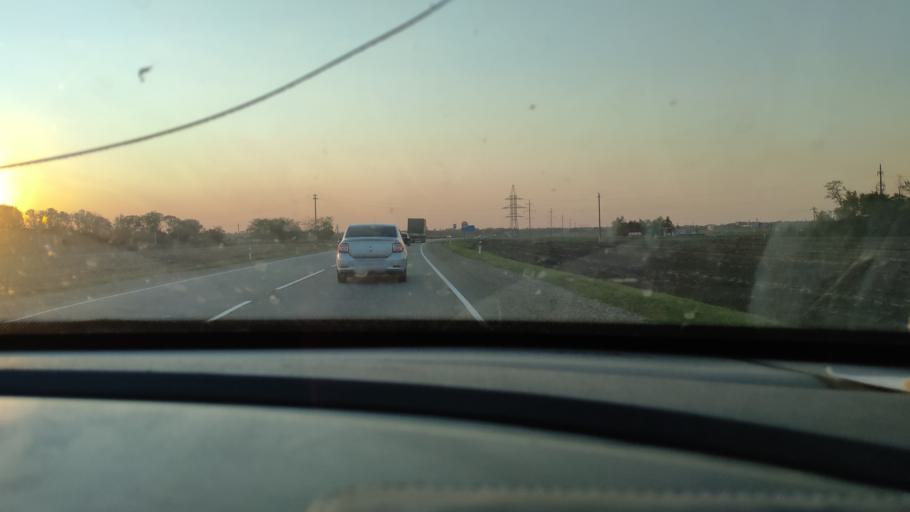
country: RU
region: Krasnodarskiy
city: Starominskaya
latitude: 46.5008
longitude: 39.0431
